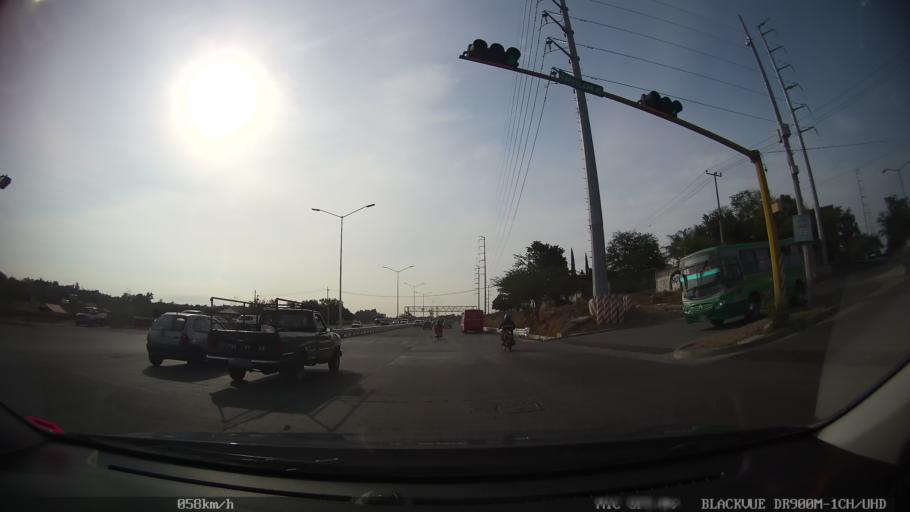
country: MX
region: Jalisco
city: Tlaquepaque
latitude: 20.6869
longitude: -103.2593
